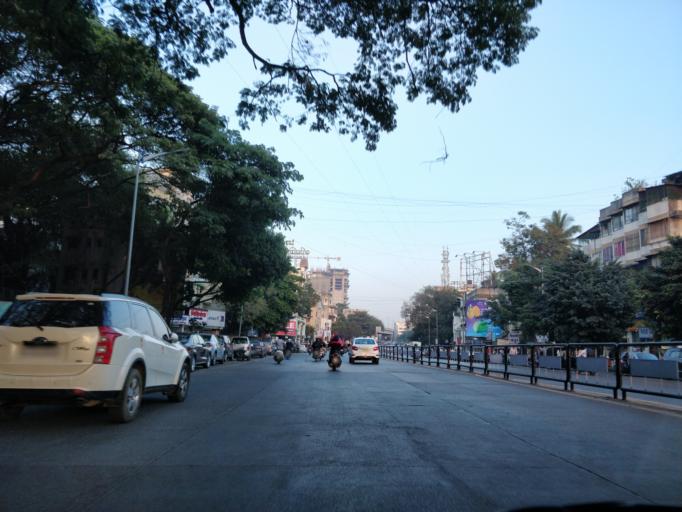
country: IN
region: Maharashtra
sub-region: Pune Division
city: Pune
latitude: 18.5048
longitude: 73.8222
